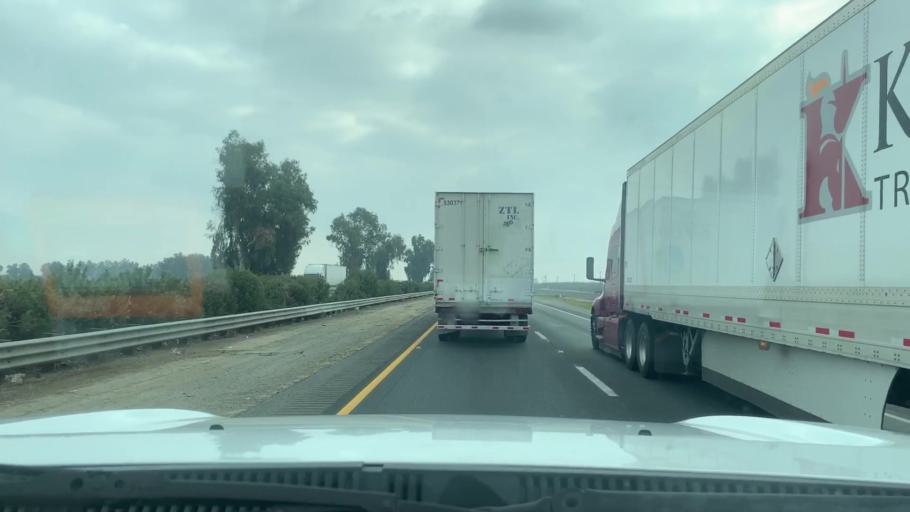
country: US
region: California
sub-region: Tulare County
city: Tipton
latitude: 36.0313
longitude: -119.3081
